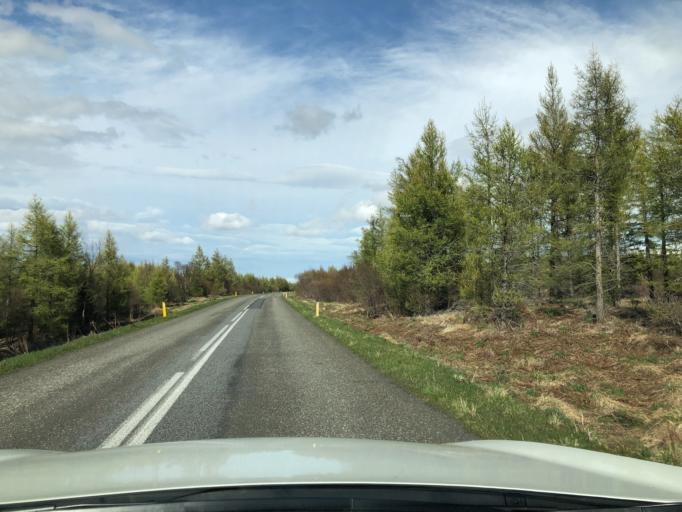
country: IS
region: East
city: Egilsstadir
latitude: 65.1414
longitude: -14.6661
